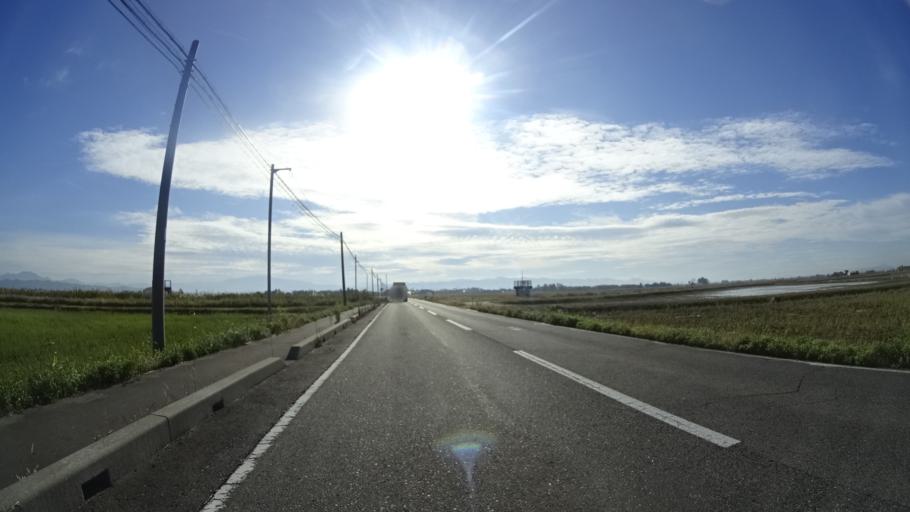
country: JP
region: Niigata
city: Mitsuke
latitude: 37.5661
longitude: 138.8459
